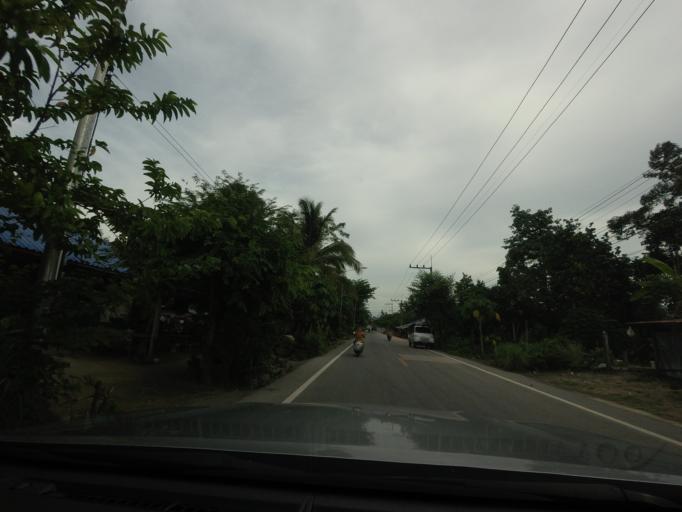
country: TH
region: Narathiwat
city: Rueso
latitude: 6.4014
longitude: 101.4556
